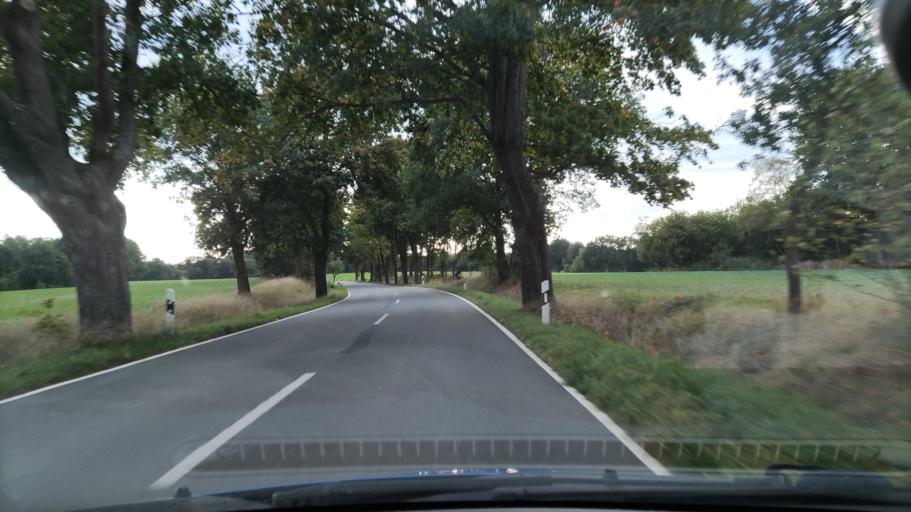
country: DE
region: Mecklenburg-Vorpommern
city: Boizenburg
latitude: 53.4133
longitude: 10.8432
